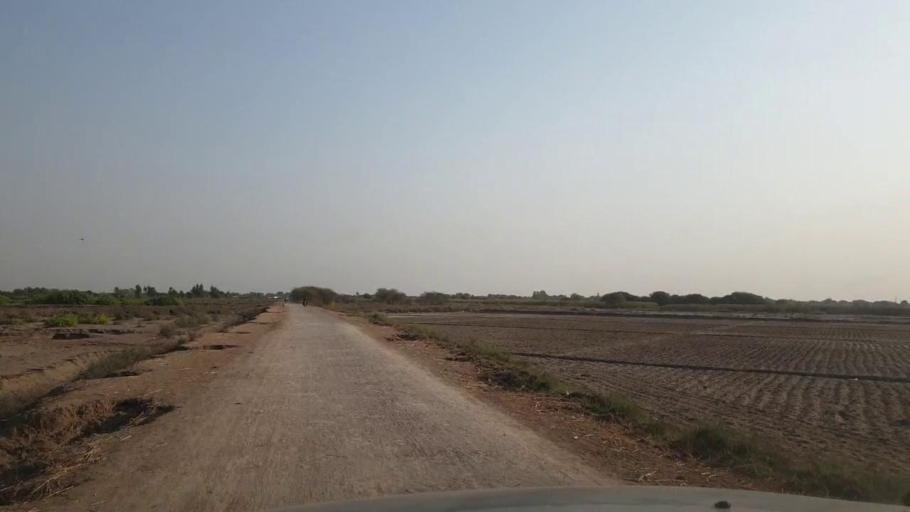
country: PK
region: Sindh
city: Bulri
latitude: 24.9504
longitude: 68.3414
